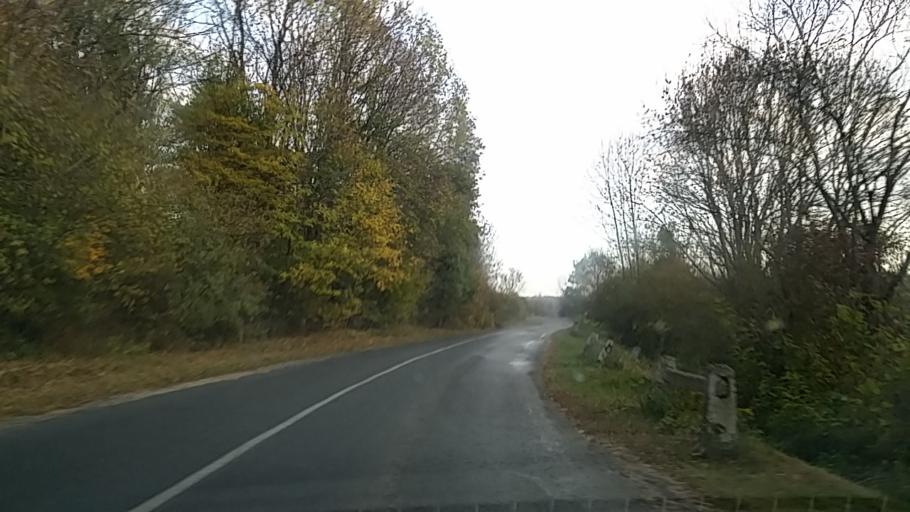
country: HU
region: Veszprem
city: Zirc
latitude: 47.2285
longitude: 17.8088
